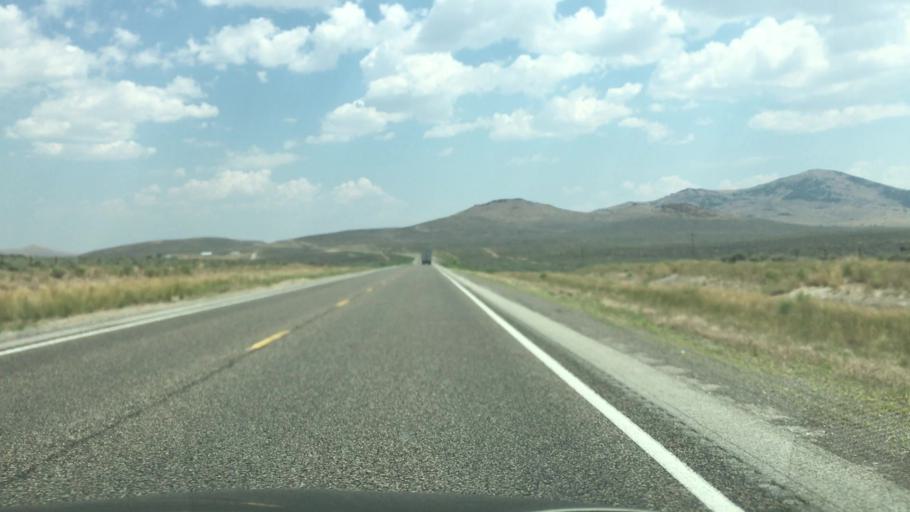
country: US
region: Nevada
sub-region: Elko County
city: Wells
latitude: 41.1666
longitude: -114.8871
